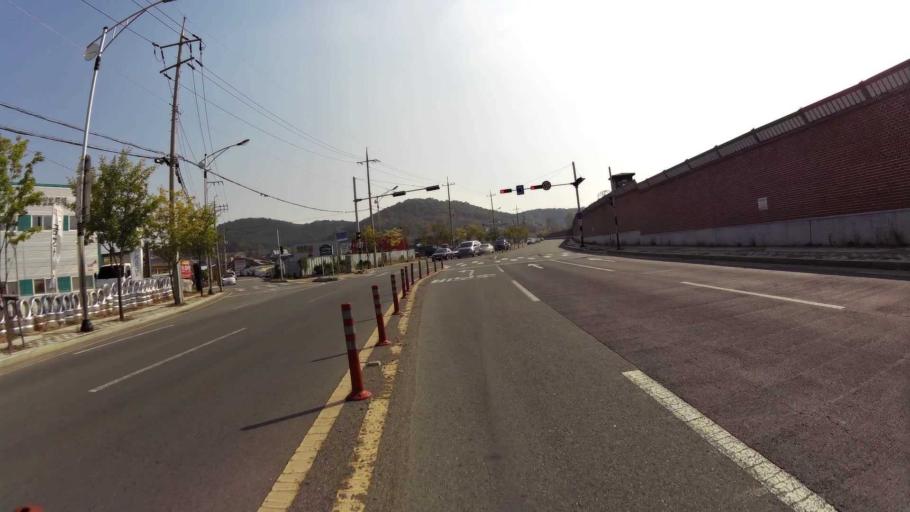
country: KR
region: Gyeongsangbuk-do
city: Gyeongsan-si
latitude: 35.8529
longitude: 128.6837
